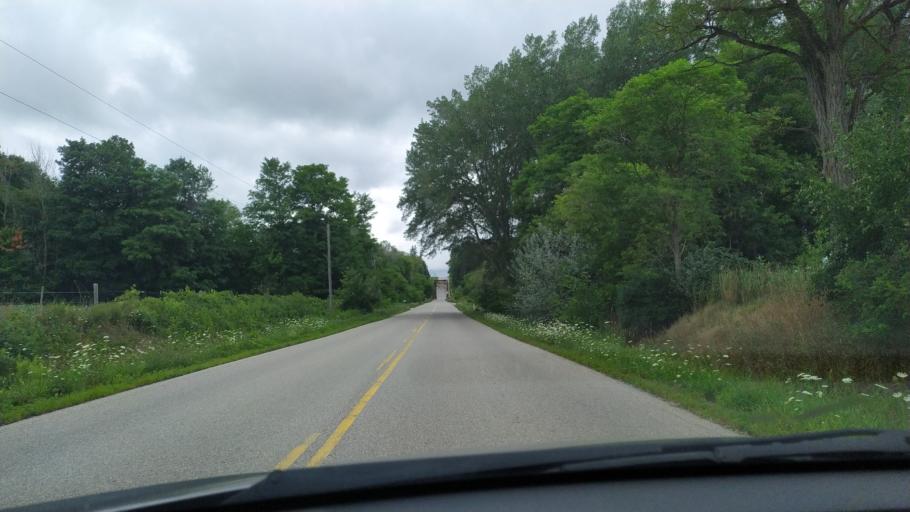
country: CA
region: Ontario
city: Kitchener
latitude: 43.3334
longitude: -80.6405
